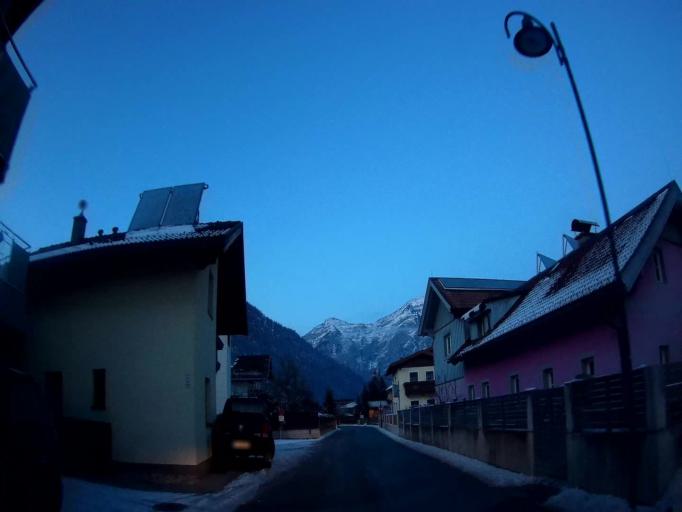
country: AT
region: Salzburg
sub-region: Politischer Bezirk Zell am See
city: Saalfelden am Steinernen Meer
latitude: 47.4444
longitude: 12.8178
